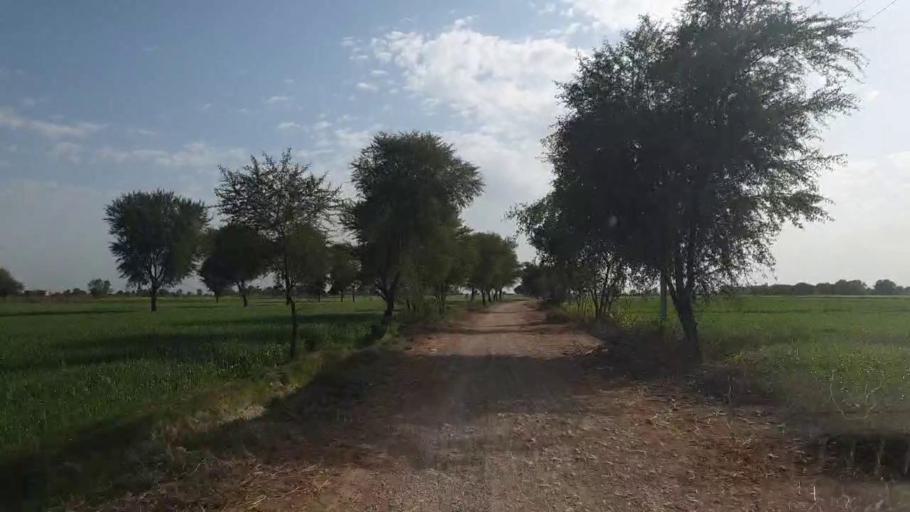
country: PK
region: Sindh
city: Shahdadpur
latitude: 26.0308
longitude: 68.4780
